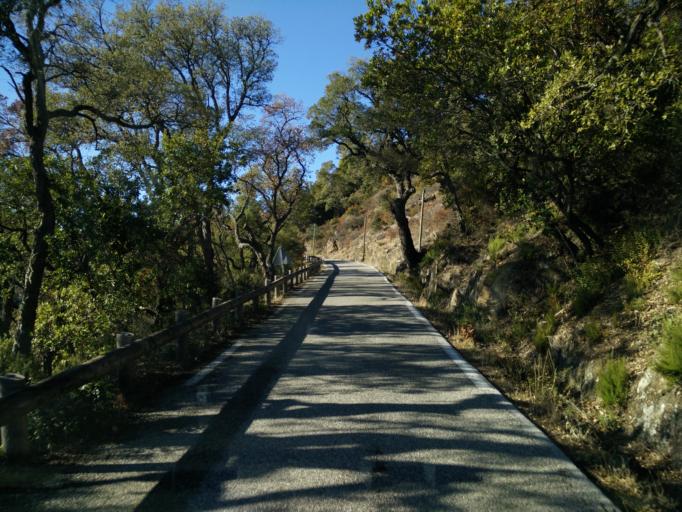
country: FR
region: Provence-Alpes-Cote d'Azur
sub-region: Departement du Var
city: La Garde-Freinet
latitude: 43.2573
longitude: 6.4349
